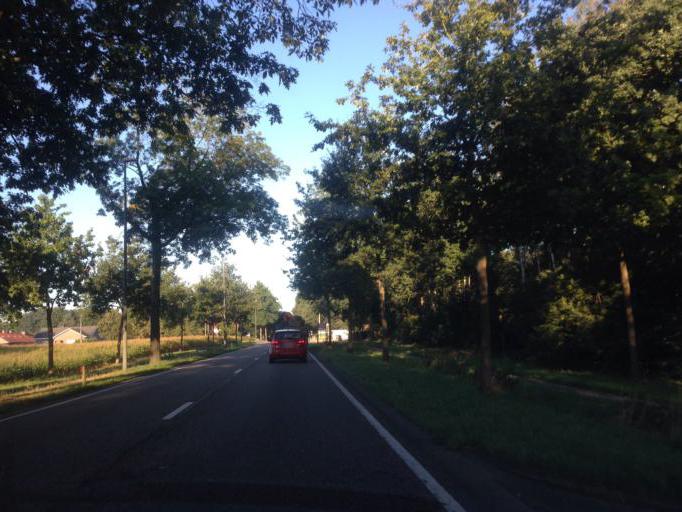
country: BE
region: Flanders
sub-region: Provincie Limburg
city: Peer
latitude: 51.1277
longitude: 5.3949
